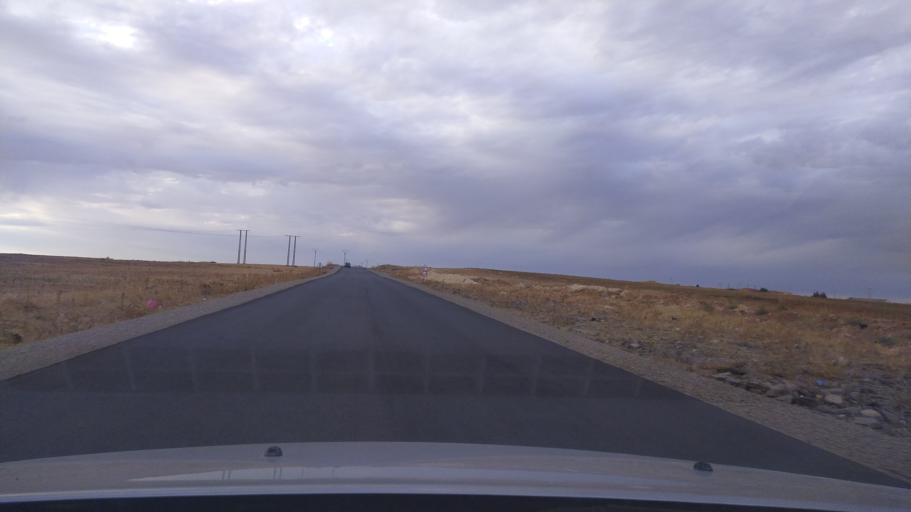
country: DZ
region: Tiaret
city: Frenda
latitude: 35.0031
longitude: 1.1234
